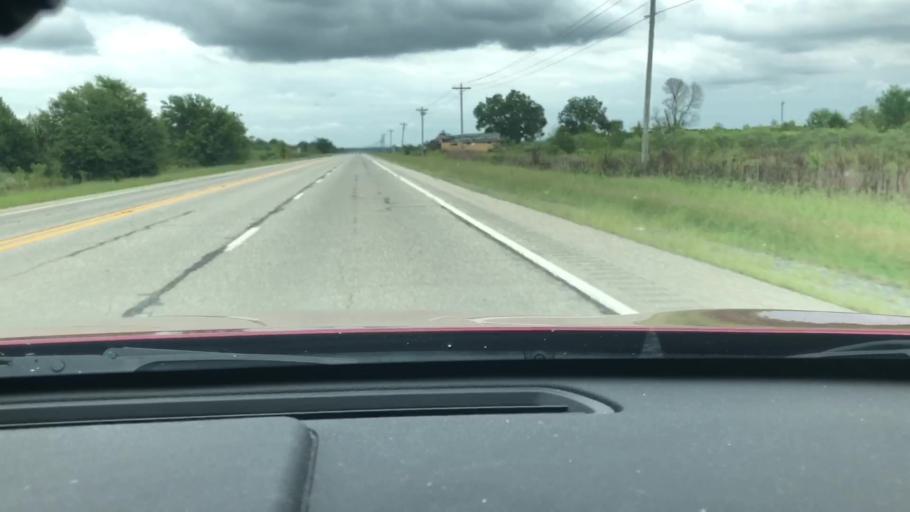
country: US
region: Arkansas
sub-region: Lafayette County
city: Lewisville
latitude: 33.4127
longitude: -93.7978
